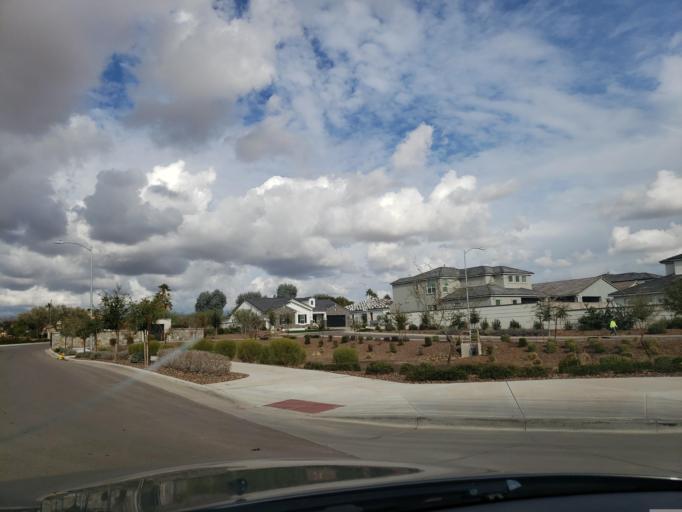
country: US
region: Arizona
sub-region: Maricopa County
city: Paradise Valley
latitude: 33.6466
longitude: -111.9735
